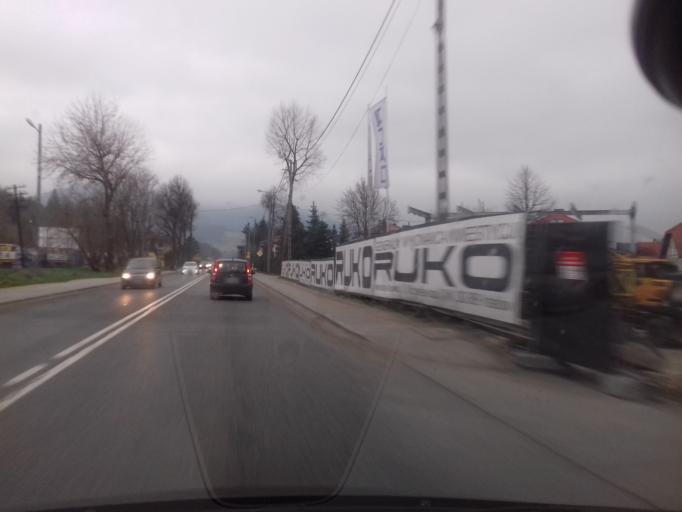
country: PL
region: Lesser Poland Voivodeship
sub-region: Powiat limanowski
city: Mszana Dolna
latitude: 49.6738
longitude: 20.0750
